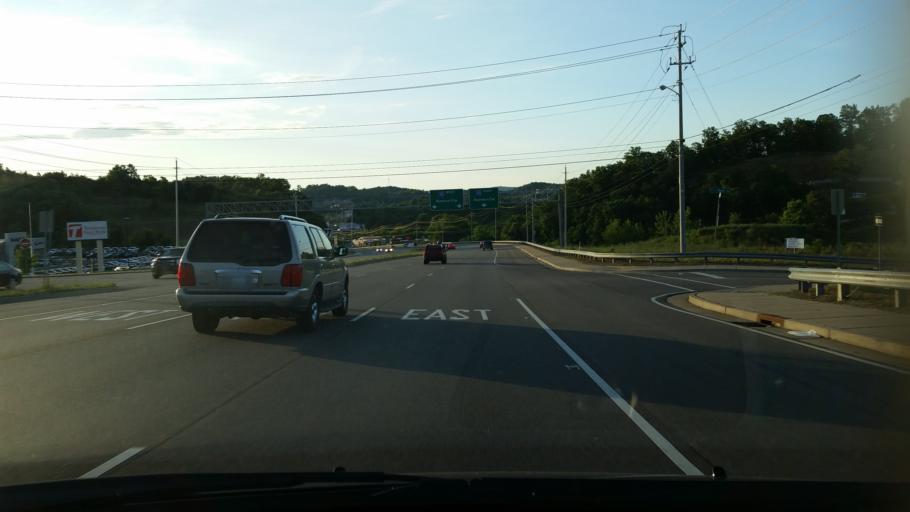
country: US
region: Tennessee
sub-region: Sevier County
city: Sevierville
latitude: 35.9712
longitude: -83.6025
